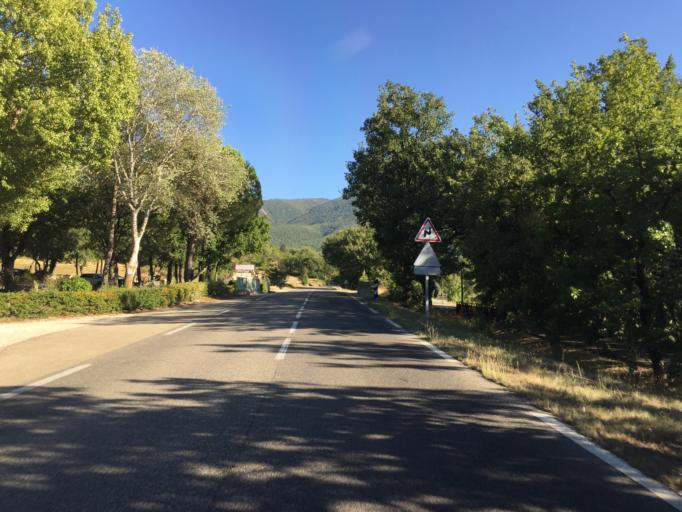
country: FR
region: Provence-Alpes-Cote d'Azur
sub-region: Departement du Vaucluse
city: Saignon
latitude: 43.8567
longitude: 5.4761
